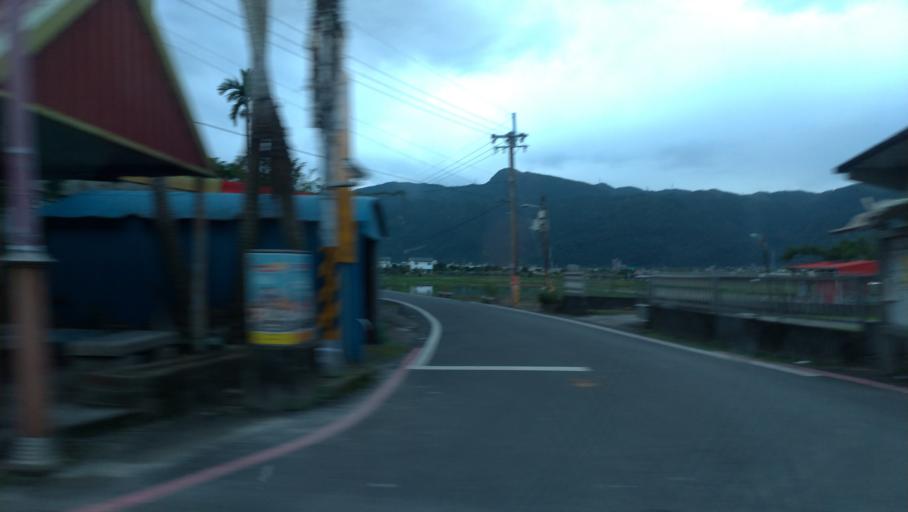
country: TW
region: Taiwan
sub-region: Yilan
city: Yilan
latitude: 24.8348
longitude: 121.8037
